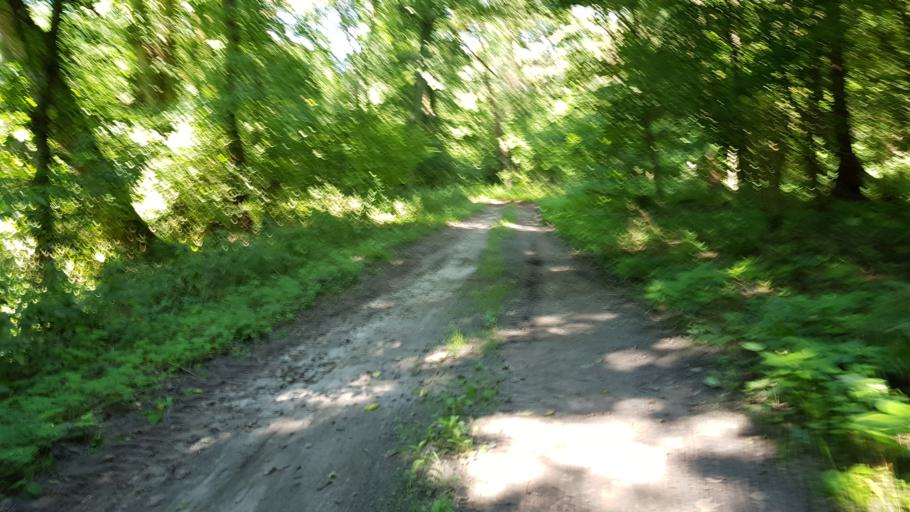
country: PL
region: West Pomeranian Voivodeship
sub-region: Powiat gryfinski
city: Banie
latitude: 53.1582
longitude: 14.6200
